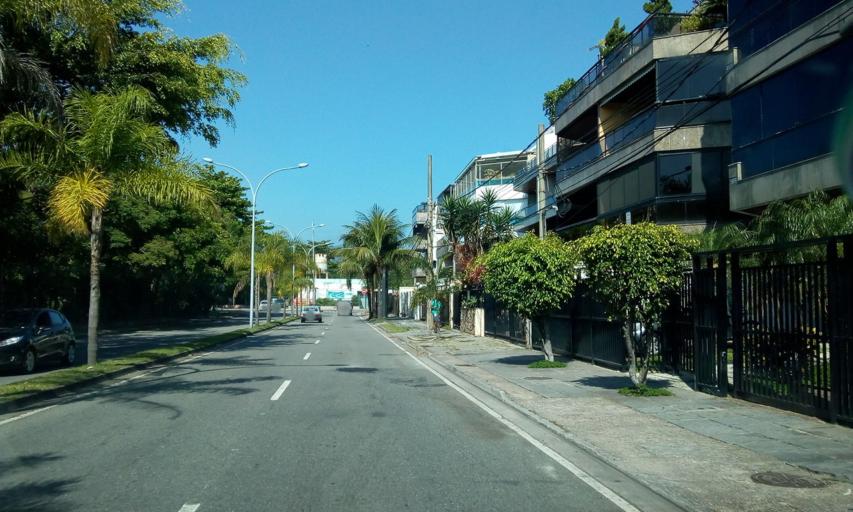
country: BR
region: Rio de Janeiro
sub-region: Nilopolis
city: Nilopolis
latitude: -23.0219
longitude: -43.4571
